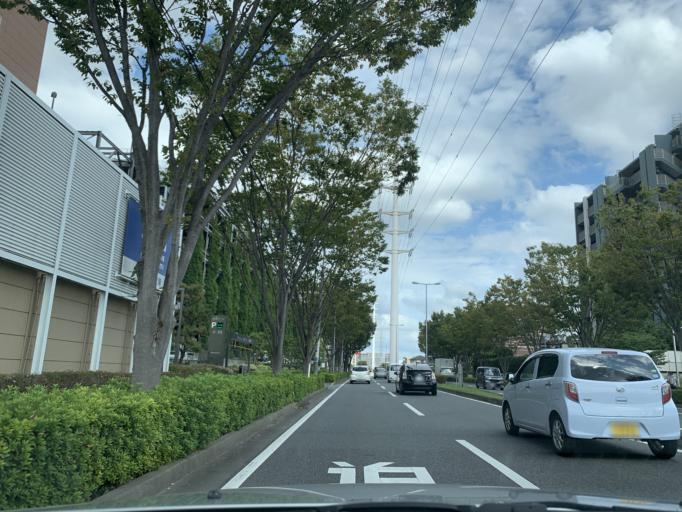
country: JP
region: Chiba
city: Nagareyama
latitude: 35.8693
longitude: 139.9261
